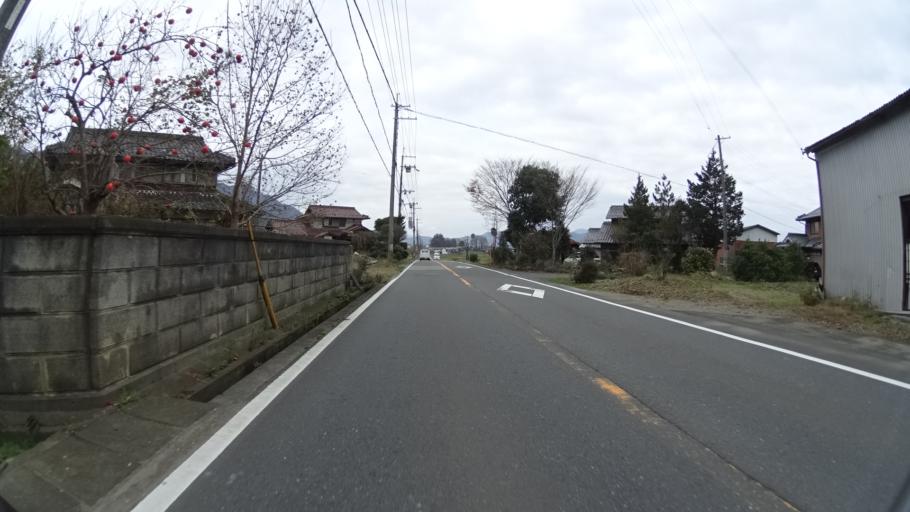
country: JP
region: Hyogo
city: Sasayama
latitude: 35.1470
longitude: 135.1237
